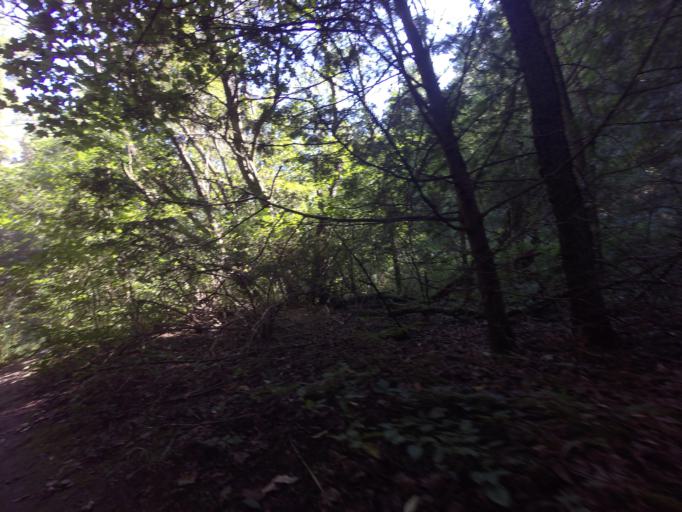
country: CA
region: Ontario
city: Waterloo
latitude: 43.6801
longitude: -80.4409
